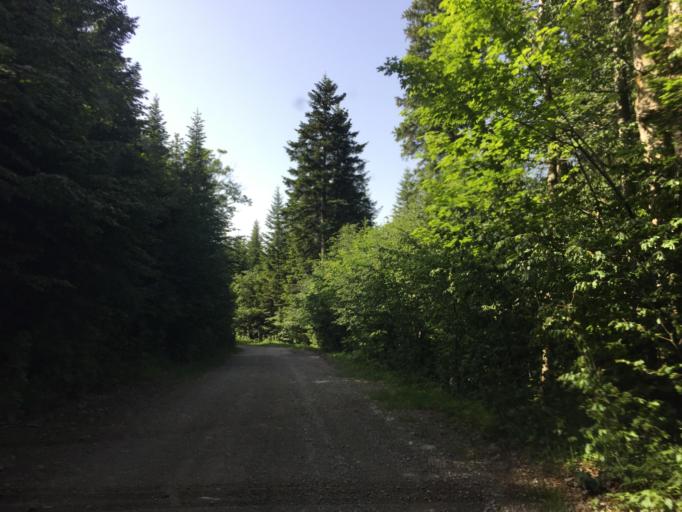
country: HR
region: Primorsko-Goranska
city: Podhum
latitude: 45.4391
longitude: 14.5620
